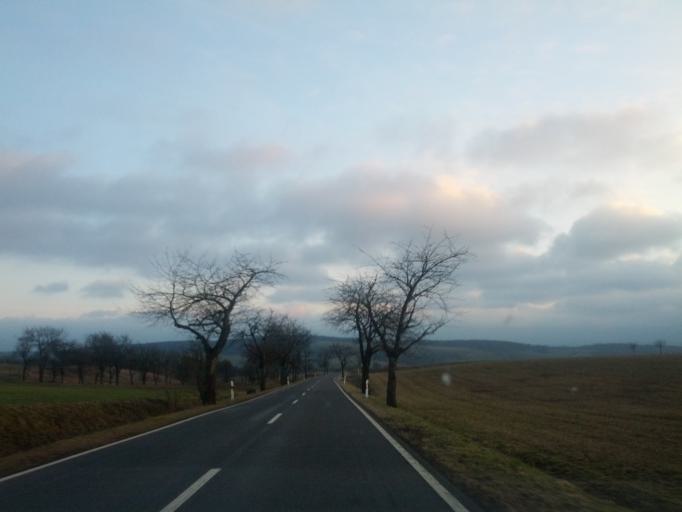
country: DE
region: Thuringia
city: Heyerode
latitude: 51.1835
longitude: 10.2951
